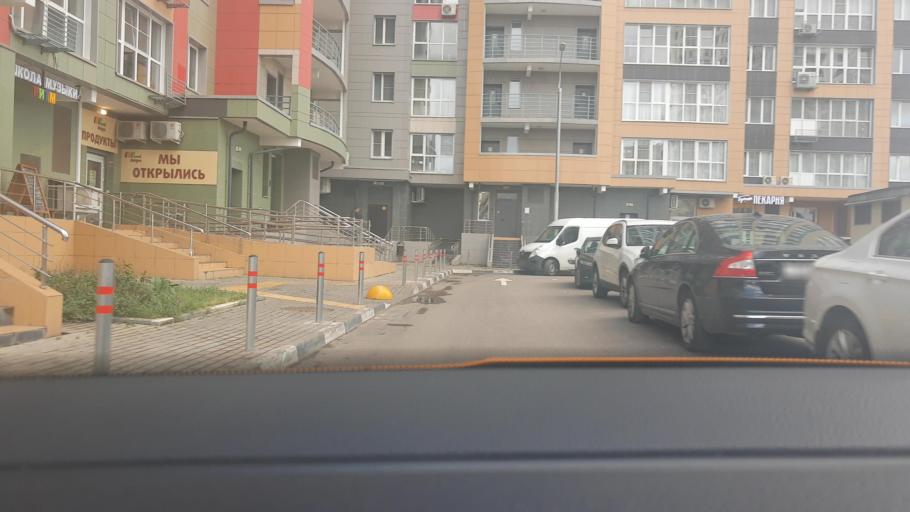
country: RU
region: Moscow
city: Amin'yevo
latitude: 55.6947
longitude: 37.4709
